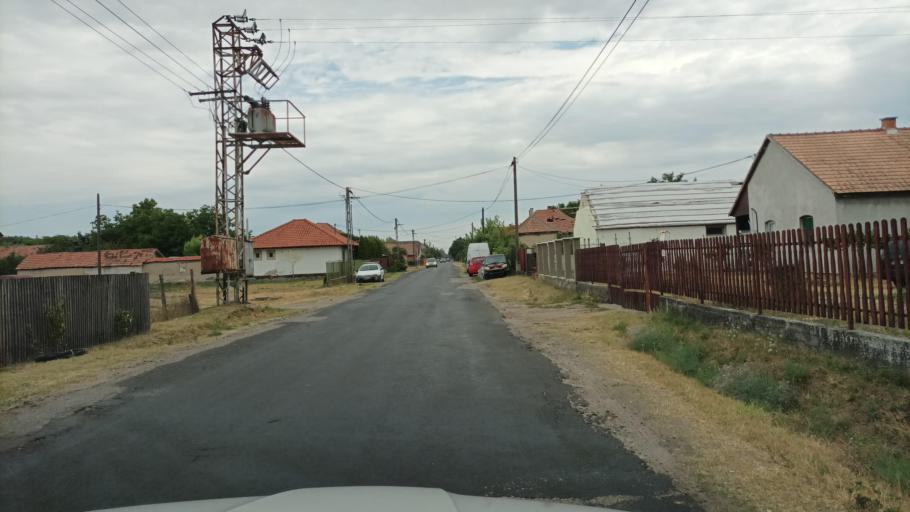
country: HU
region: Pest
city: Taborfalva
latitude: 47.1243
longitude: 19.4819
